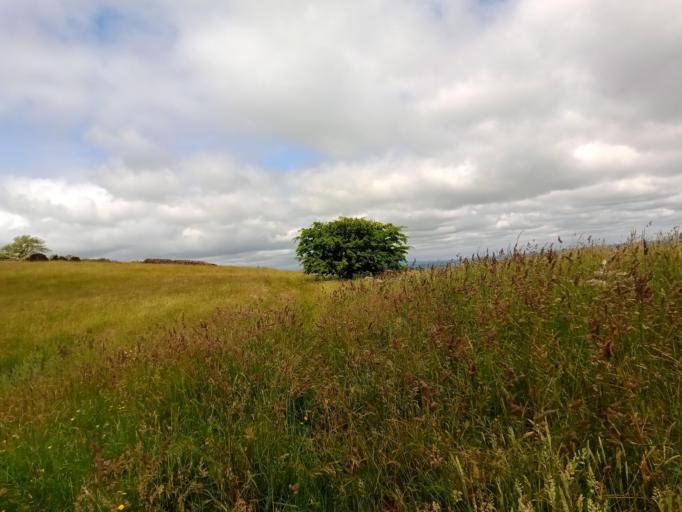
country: IE
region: Leinster
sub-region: Laois
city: Rathdowney
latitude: 52.7982
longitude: -7.4670
